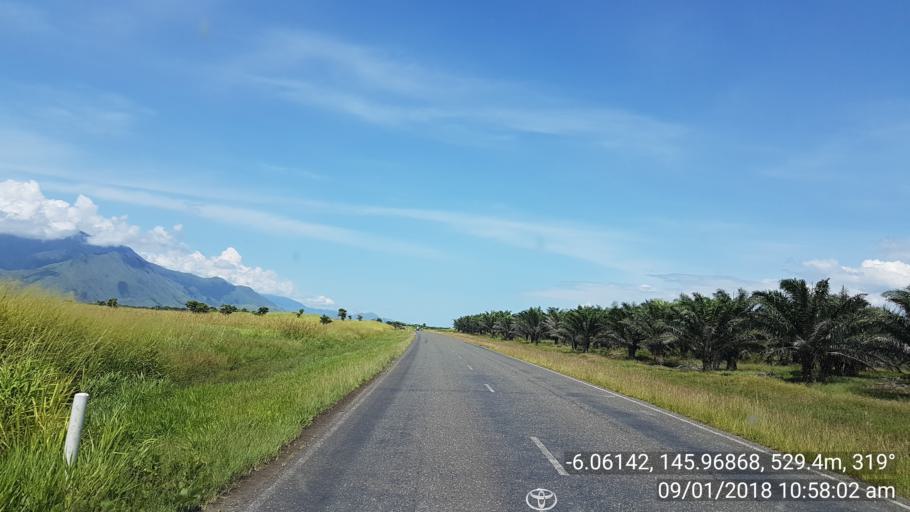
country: PG
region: Eastern Highlands
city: Kainantu
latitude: -6.0614
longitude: 145.9686
